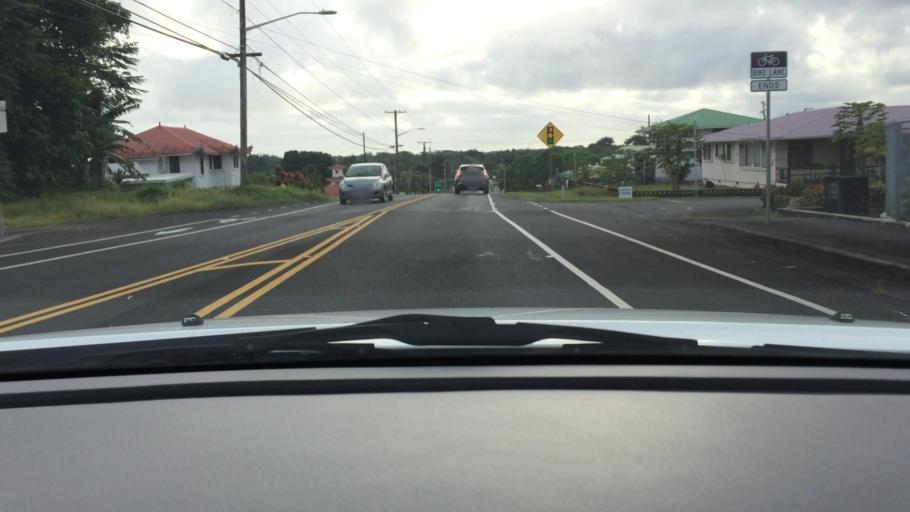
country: US
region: Hawaii
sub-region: Hawaii County
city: Hilo
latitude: 19.7109
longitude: -155.0821
